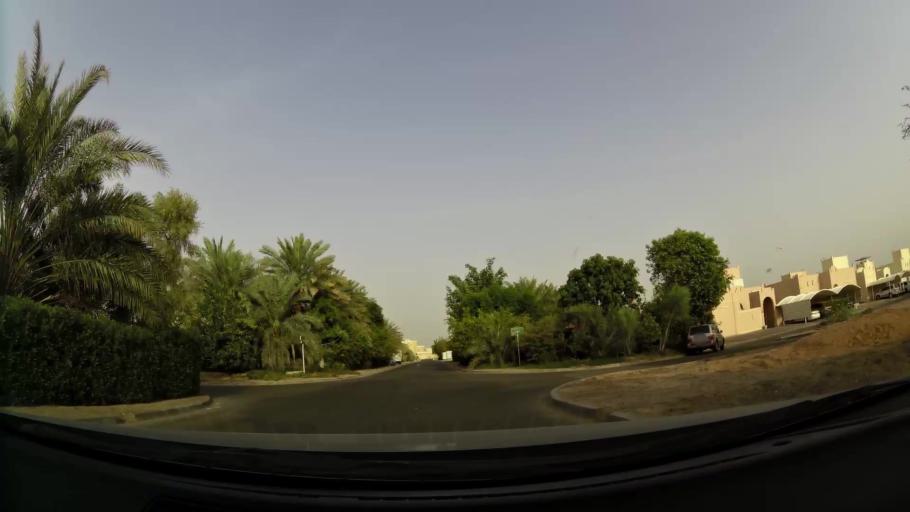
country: AE
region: Abu Dhabi
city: Al Ain
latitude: 24.1302
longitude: 55.7123
